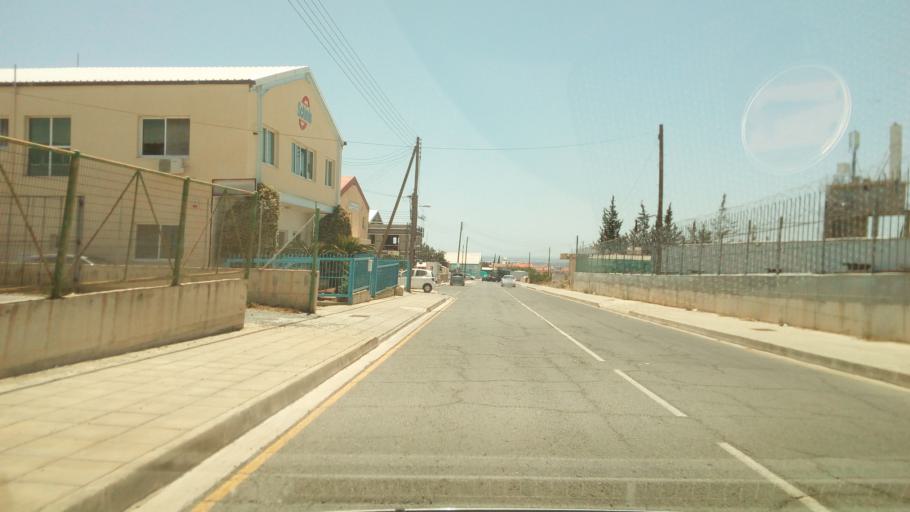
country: CY
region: Limassol
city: Ypsonas
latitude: 34.7028
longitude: 32.9559
